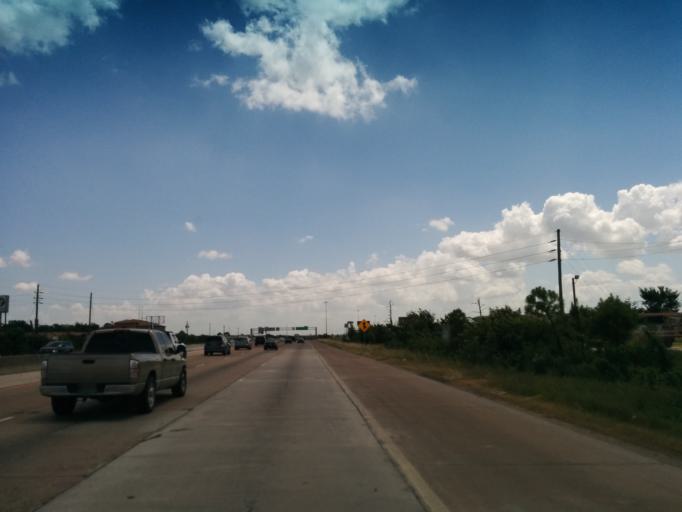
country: US
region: Texas
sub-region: Harris County
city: Channelview
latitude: 29.7882
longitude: -95.0965
